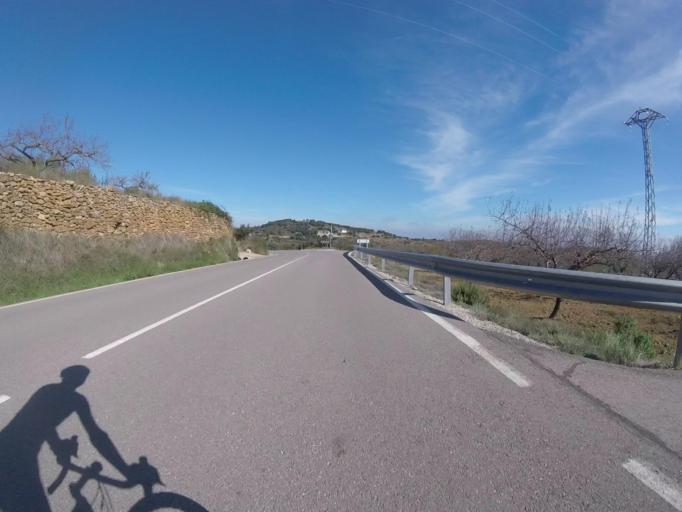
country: ES
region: Valencia
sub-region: Provincia de Castello
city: Sarratella
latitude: 40.3071
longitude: 0.0339
